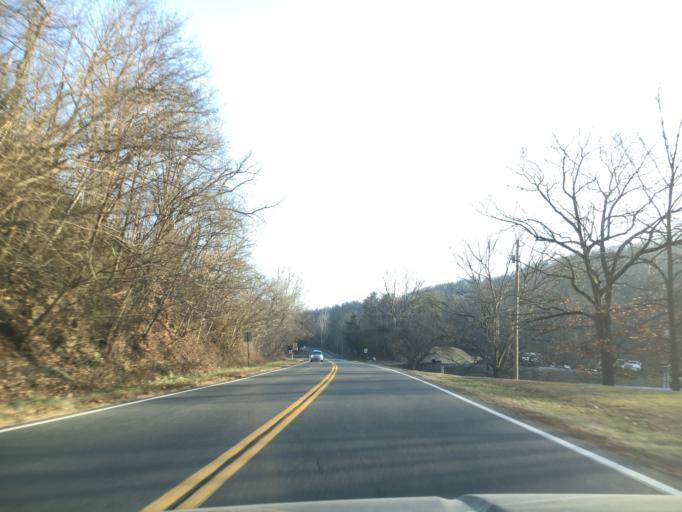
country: US
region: Virginia
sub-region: Warren County
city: Front Royal
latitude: 38.8986
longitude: -78.1815
